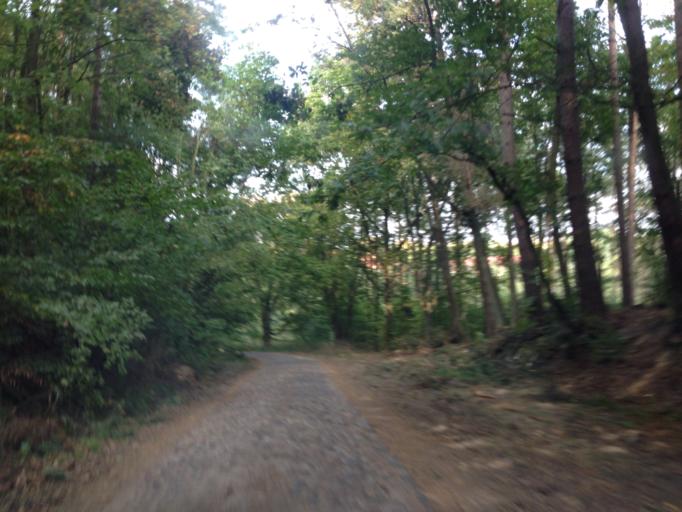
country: PL
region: Kujawsko-Pomorskie
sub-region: Powiat brodnicki
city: Gorzno
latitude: 53.2234
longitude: 19.6536
